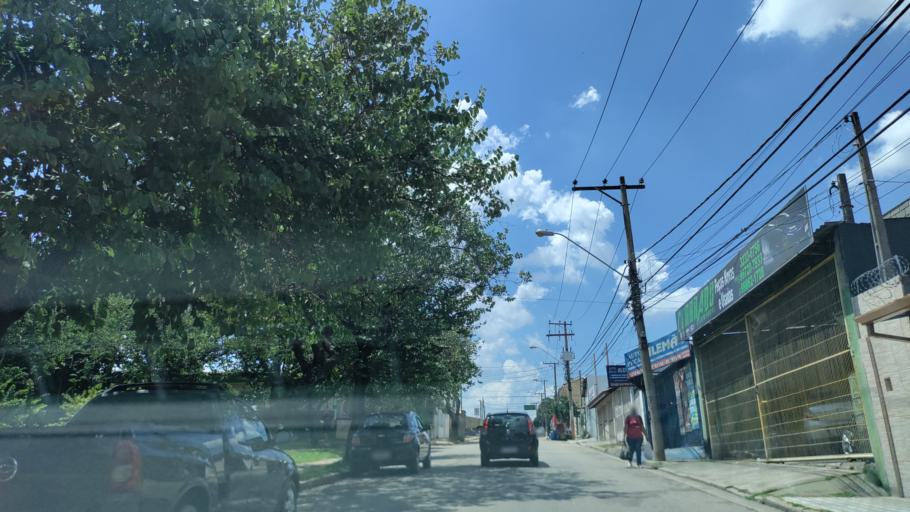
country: BR
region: Sao Paulo
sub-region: Sorocaba
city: Sorocaba
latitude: -23.4830
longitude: -47.4708
